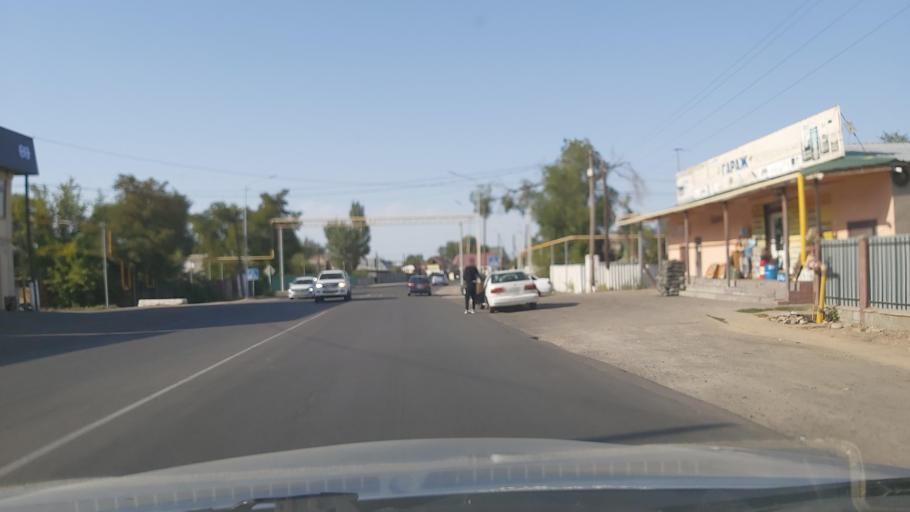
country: KZ
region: Almaty Oblysy
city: Energeticheskiy
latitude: 43.4894
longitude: 77.0342
